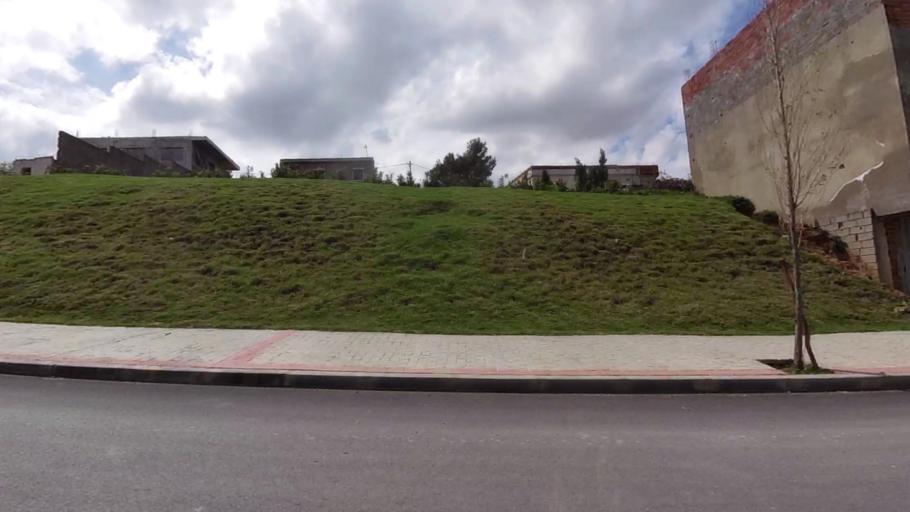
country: MA
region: Tanger-Tetouan
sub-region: Tanger-Assilah
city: Tangier
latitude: 35.7767
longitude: -5.7524
